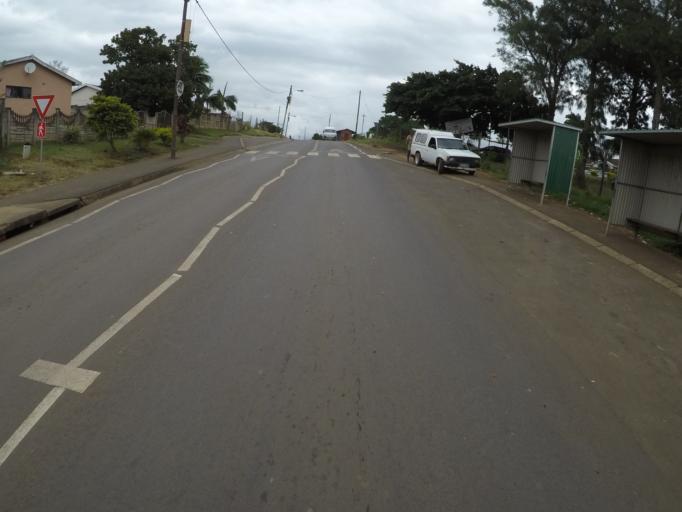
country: ZA
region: KwaZulu-Natal
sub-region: uThungulu District Municipality
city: Empangeni
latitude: -28.7829
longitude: 31.8566
